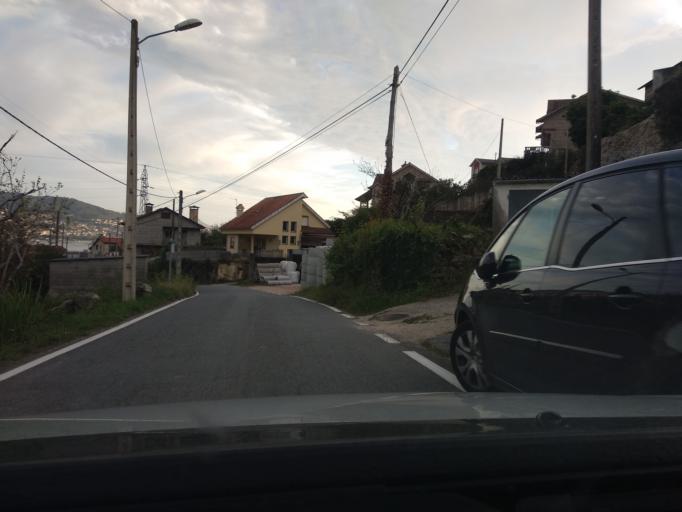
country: ES
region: Galicia
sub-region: Provincia de Pontevedra
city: Moana
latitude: 42.2939
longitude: -8.6821
